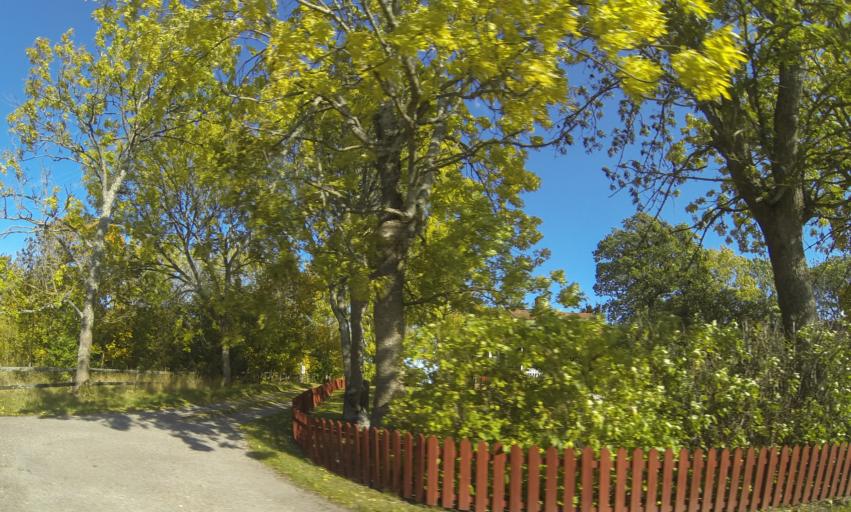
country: SE
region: Vaestmanland
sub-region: Vasteras
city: Vasteras
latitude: 59.5452
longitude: 16.4434
